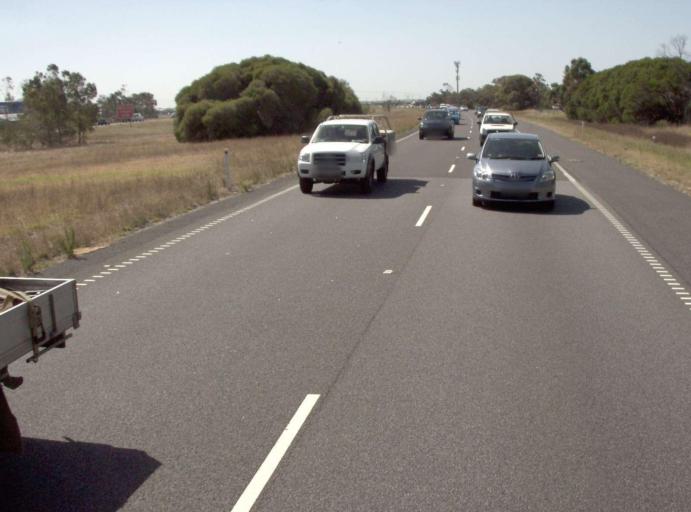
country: AU
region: Victoria
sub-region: Kingston
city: Chelsea Heights
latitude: -38.0305
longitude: 145.1371
